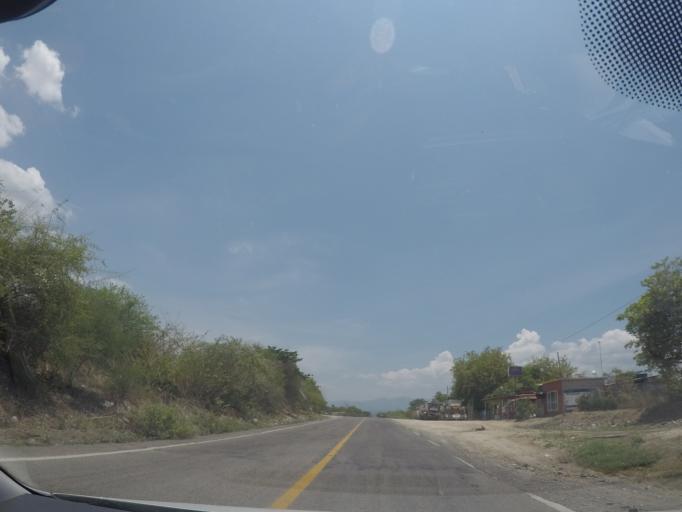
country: MX
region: Oaxaca
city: Santa Maria Jalapa del Marques
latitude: 16.4394
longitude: -95.5043
